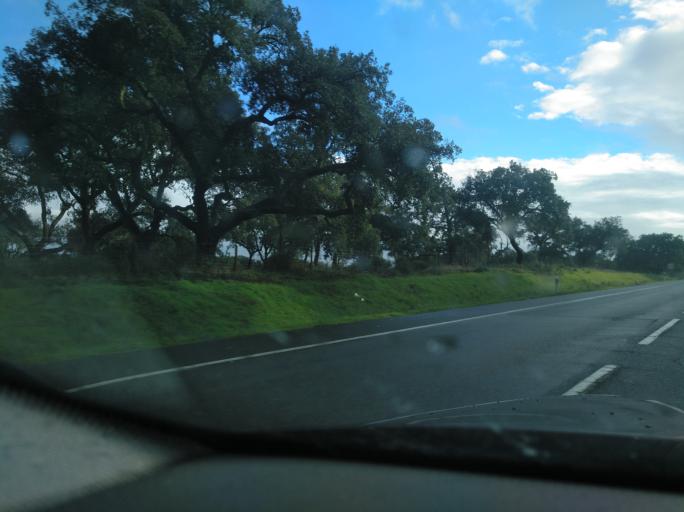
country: PT
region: Setubal
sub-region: Grandola
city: Grandola
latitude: 38.0285
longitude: -8.3999
